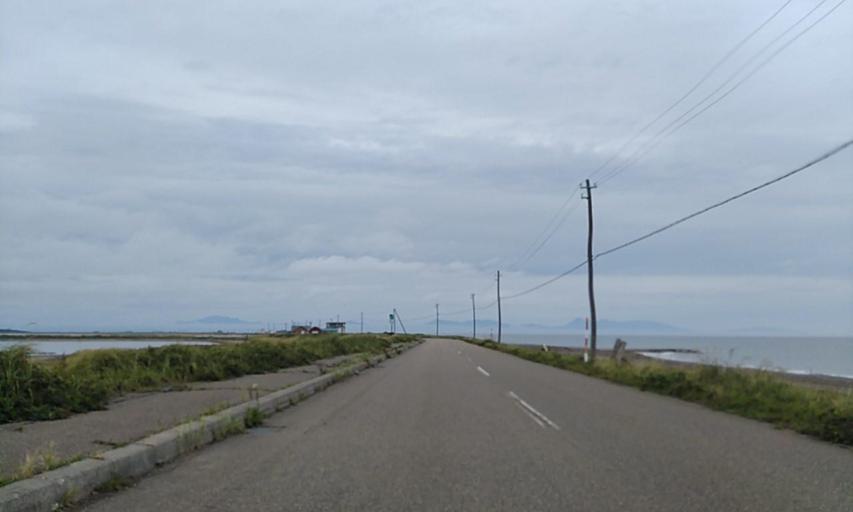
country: JP
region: Hokkaido
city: Shibetsu
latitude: 43.5859
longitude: 145.3403
